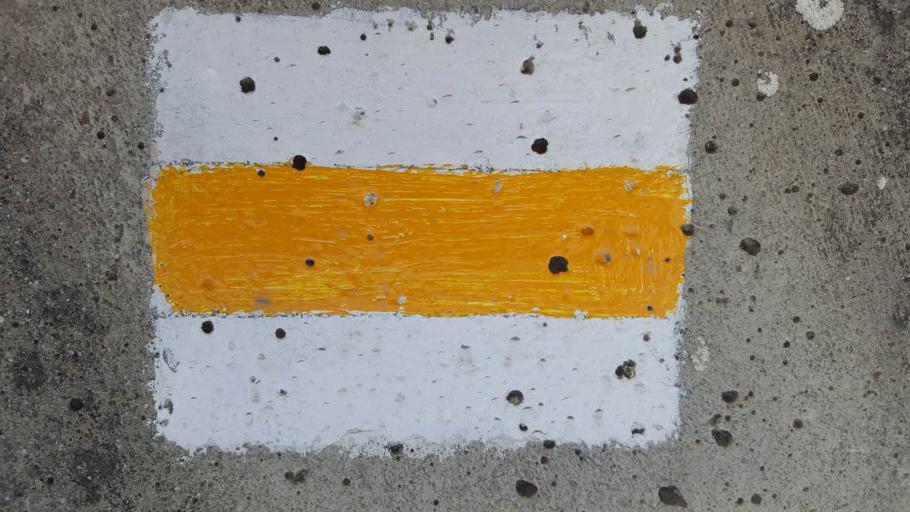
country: HU
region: Somogy
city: Somogyvar
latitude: 46.5828
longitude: 17.6681
